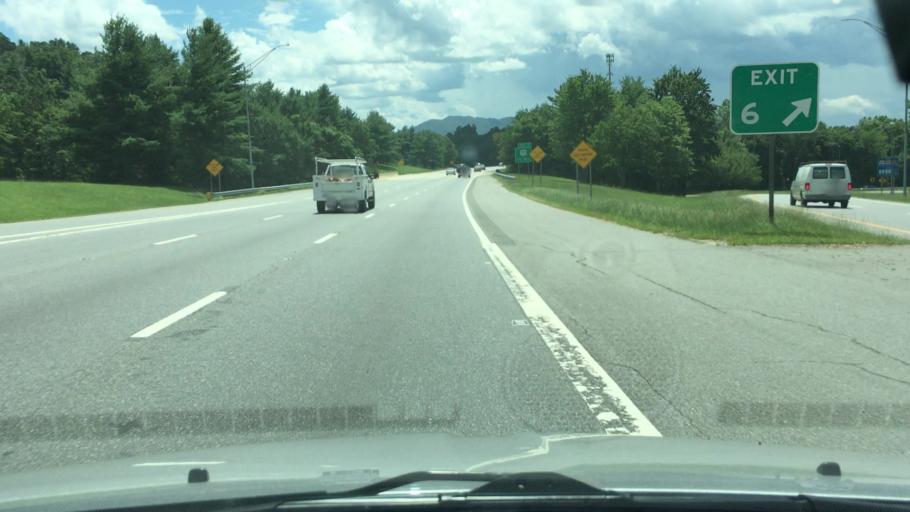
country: US
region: North Carolina
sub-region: Buncombe County
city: Asheville
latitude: 35.5950
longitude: -82.5297
